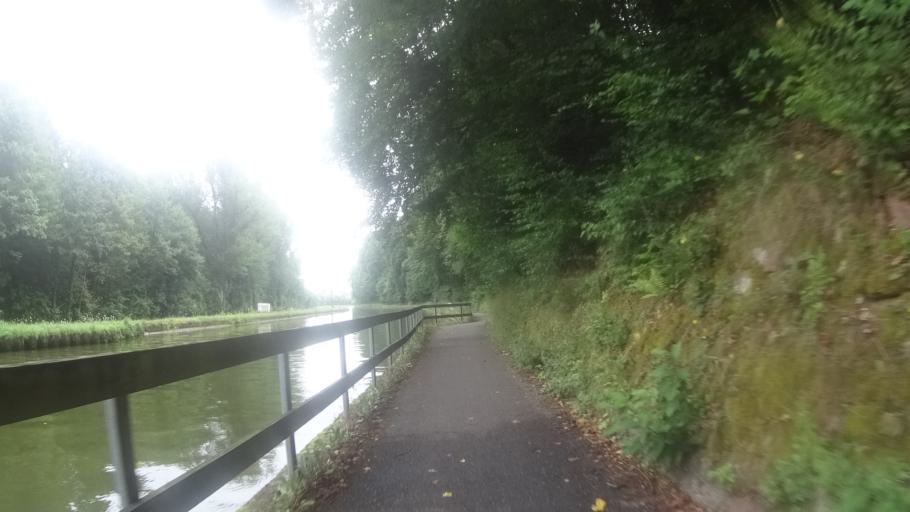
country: FR
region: Alsace
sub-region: Departement du Bas-Rhin
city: Saverne
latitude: 48.7363
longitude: 7.3454
